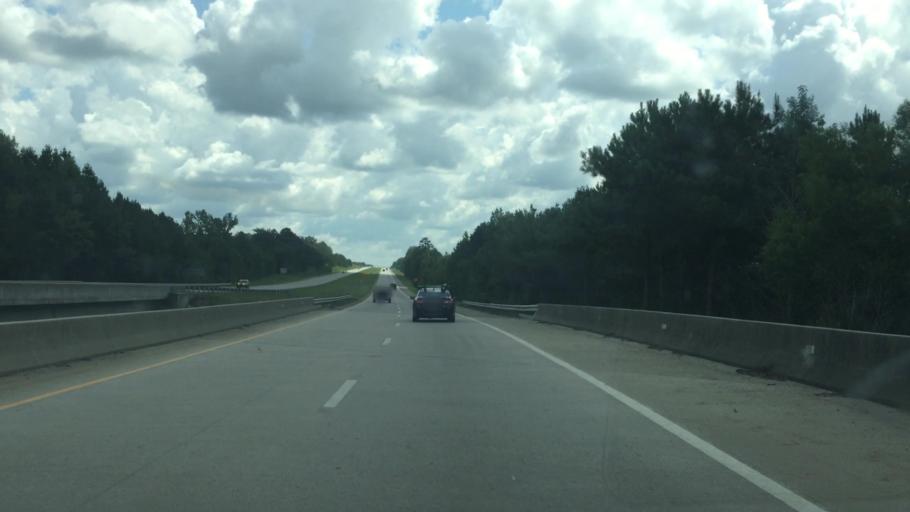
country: US
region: North Carolina
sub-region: Richmond County
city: Hamlet
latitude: 34.8522
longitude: -79.7295
